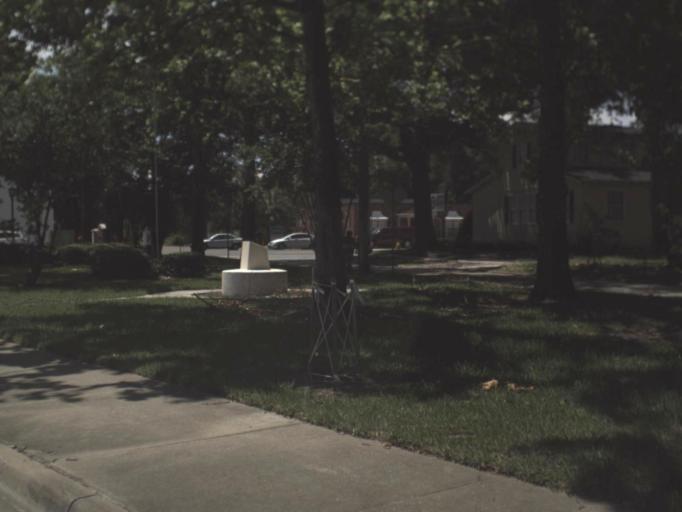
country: US
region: Florida
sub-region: Duval County
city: Jacksonville
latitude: 30.3084
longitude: -81.6477
